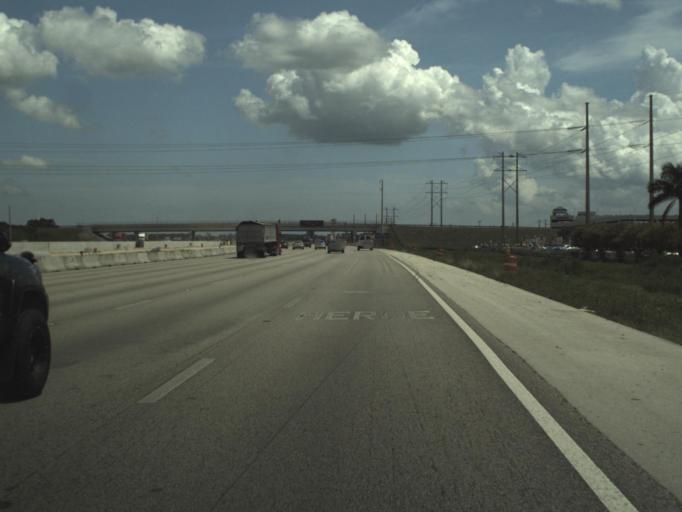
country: US
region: Florida
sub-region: Broward County
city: Southwest Ranches
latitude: 26.0783
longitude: -80.3614
